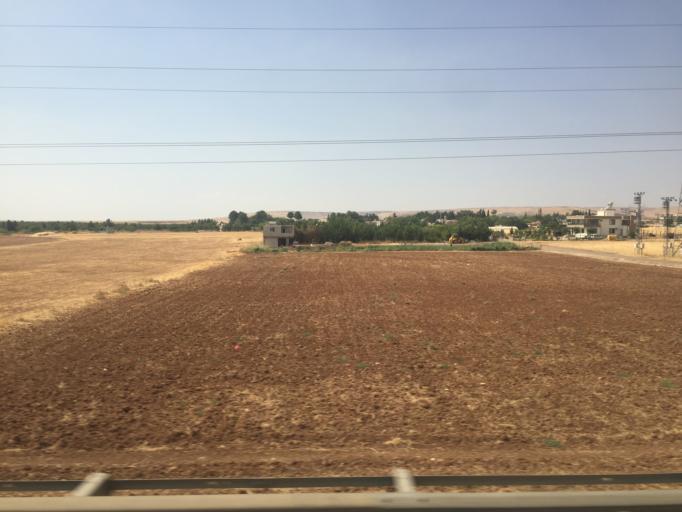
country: TR
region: Sanliurfa
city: Akziyaret
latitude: 37.3846
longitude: 38.8534
